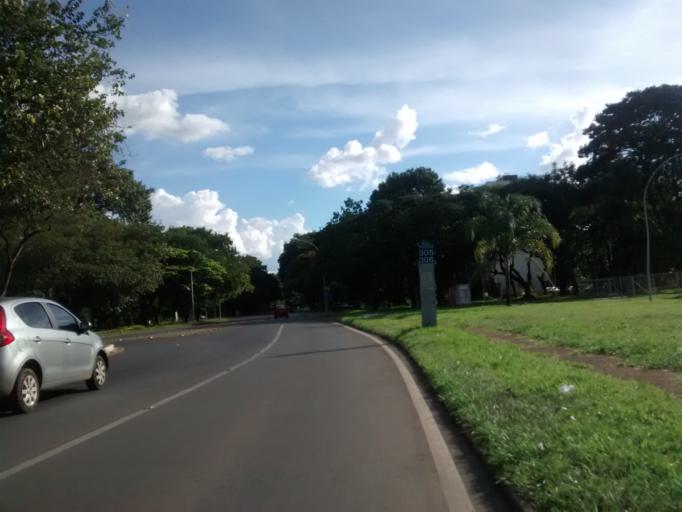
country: BR
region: Federal District
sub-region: Brasilia
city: Brasilia
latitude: -15.8104
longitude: -47.8984
